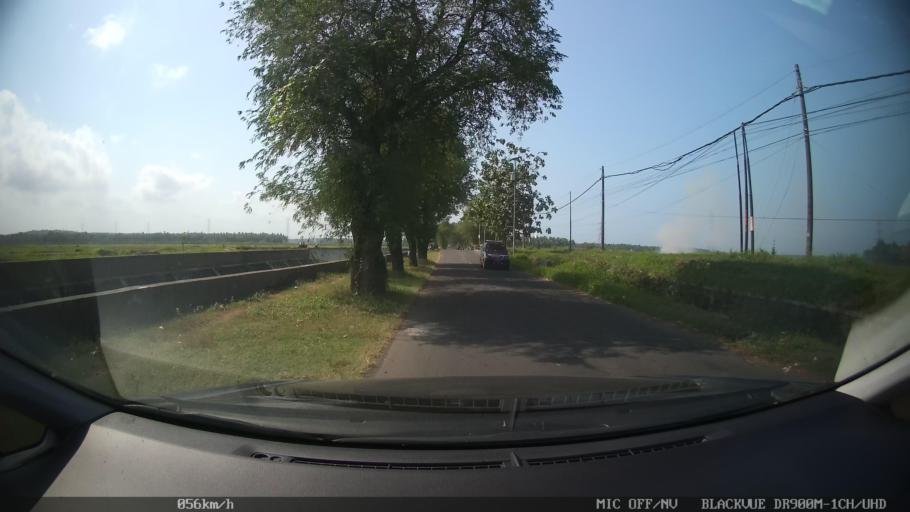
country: ID
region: Daerah Istimewa Yogyakarta
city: Srandakan
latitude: -7.9134
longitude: 110.1774
